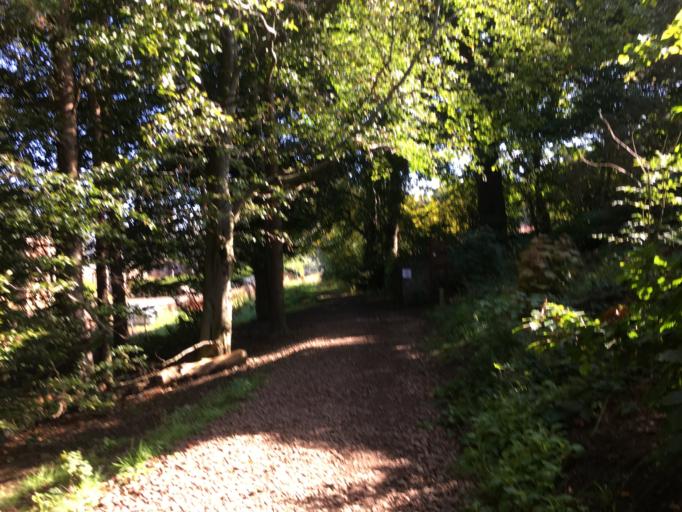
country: GB
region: Scotland
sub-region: Edinburgh
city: Colinton
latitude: 55.9223
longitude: -3.2313
